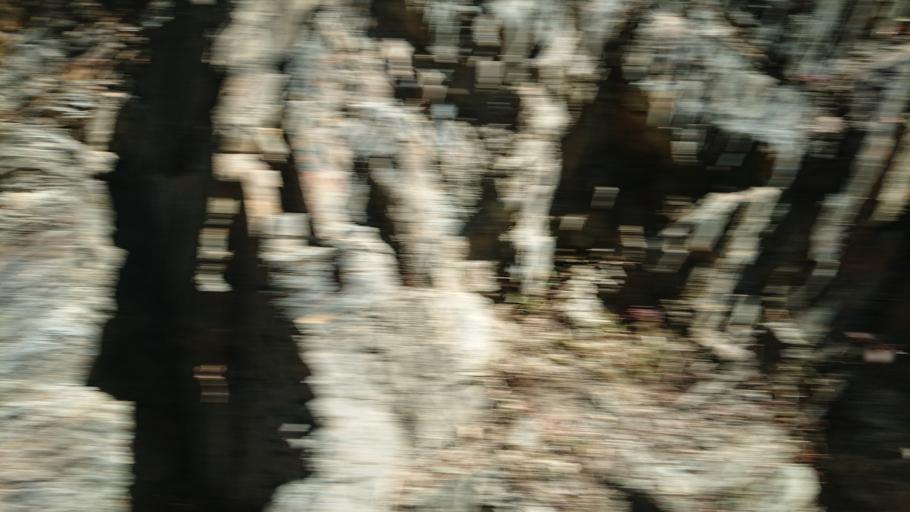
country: TW
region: Taiwan
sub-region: Hualien
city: Hualian
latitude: 24.3734
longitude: 121.3390
